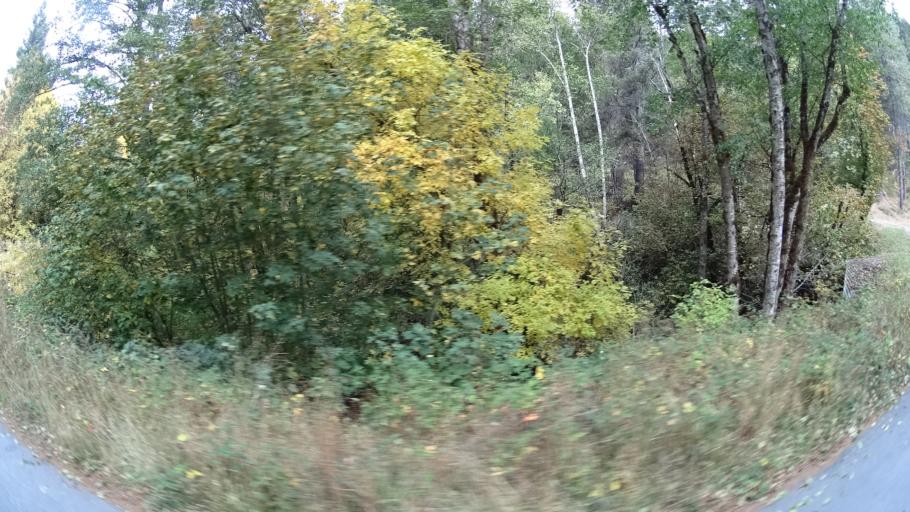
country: US
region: California
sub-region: Siskiyou County
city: Happy Camp
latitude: 41.7941
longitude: -123.3044
